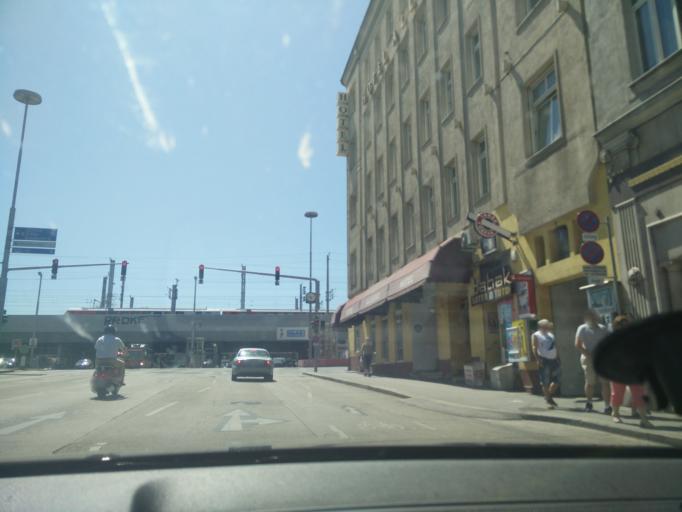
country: AT
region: Vienna
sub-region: Wien Stadt
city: Vienna
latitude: 48.1813
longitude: 16.3584
